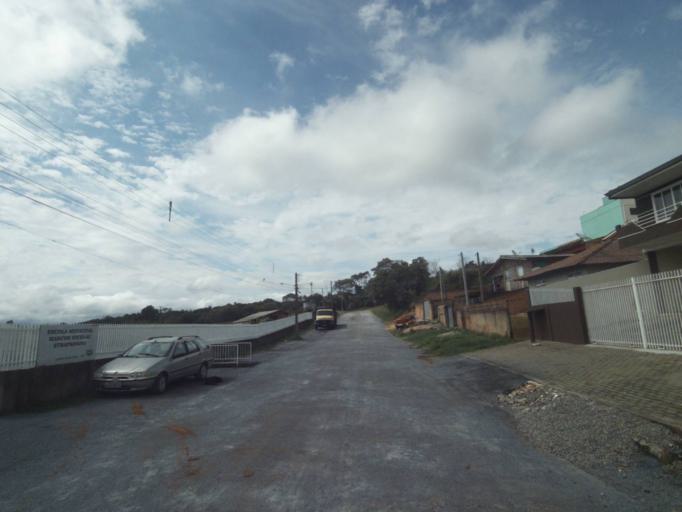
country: BR
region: Parana
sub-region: Quatro Barras
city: Quatro Barras
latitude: -25.3454
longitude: -49.0833
